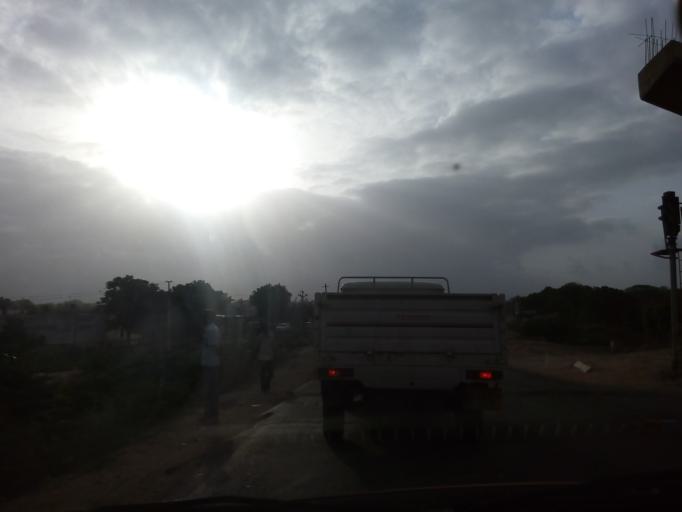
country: IN
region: Gujarat
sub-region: Kachchh
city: Bhuj
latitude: 23.2320
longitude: 69.7465
